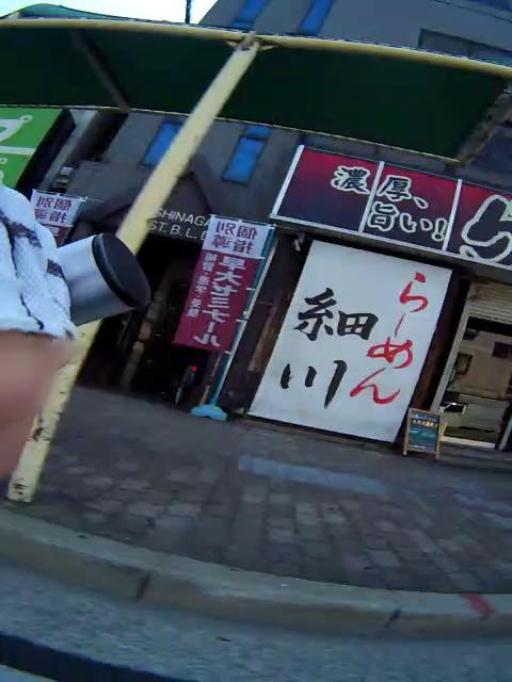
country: JP
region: Osaka
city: Yao
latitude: 34.6434
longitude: 135.5534
